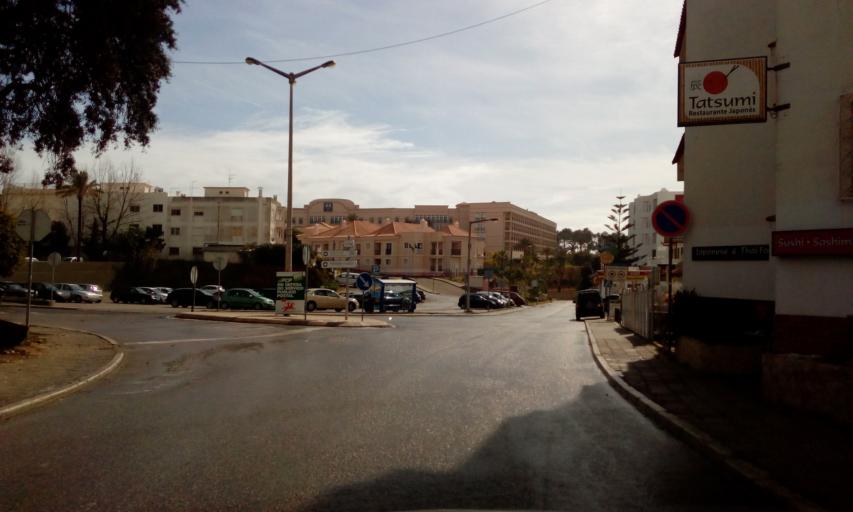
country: PT
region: Faro
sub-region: Loule
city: Boliqueime
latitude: 37.0938
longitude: -8.1877
